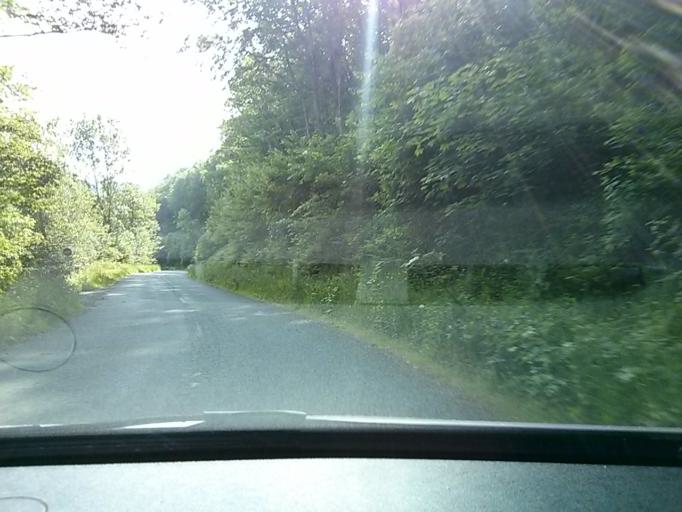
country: FR
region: Rhone-Alpes
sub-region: Departement de la Loire
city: Saint-Chamond
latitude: 45.4244
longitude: 4.5223
